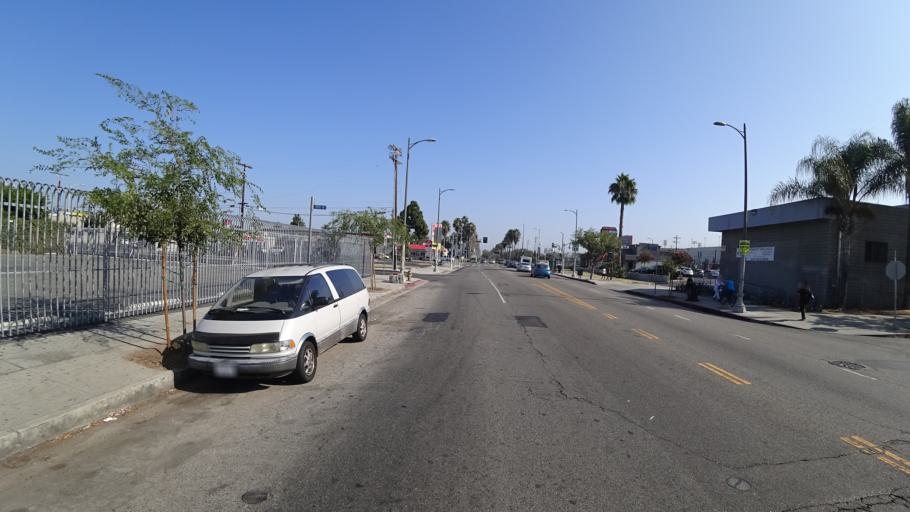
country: US
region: California
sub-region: Los Angeles County
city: View Park-Windsor Hills
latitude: 34.0099
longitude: -118.2916
